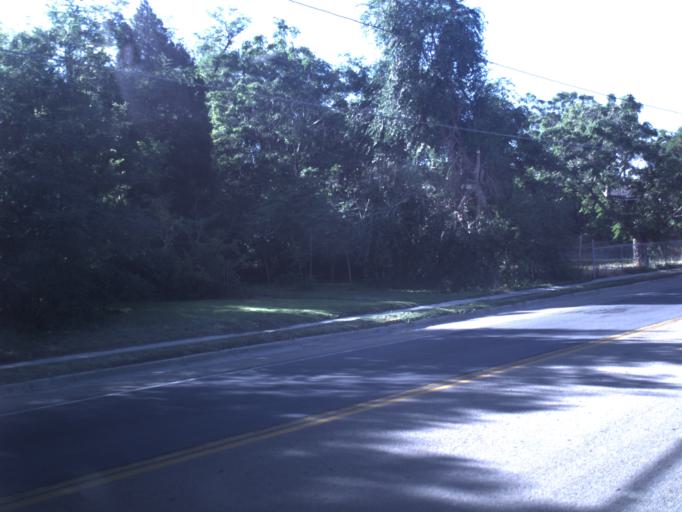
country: US
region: Utah
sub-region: Salt Lake County
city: Magna
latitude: 40.7046
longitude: -112.0919
